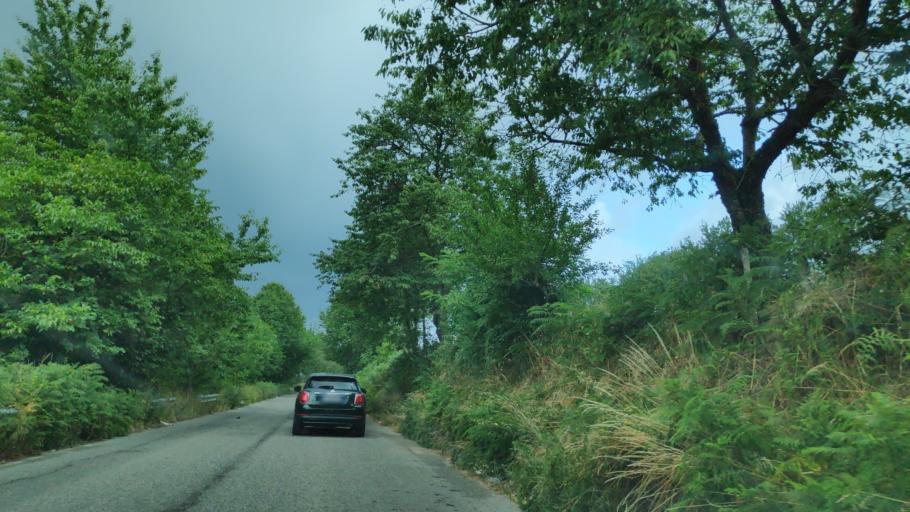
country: IT
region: Calabria
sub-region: Provincia di Vibo-Valentia
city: Mongiana
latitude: 38.5349
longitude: 16.3188
